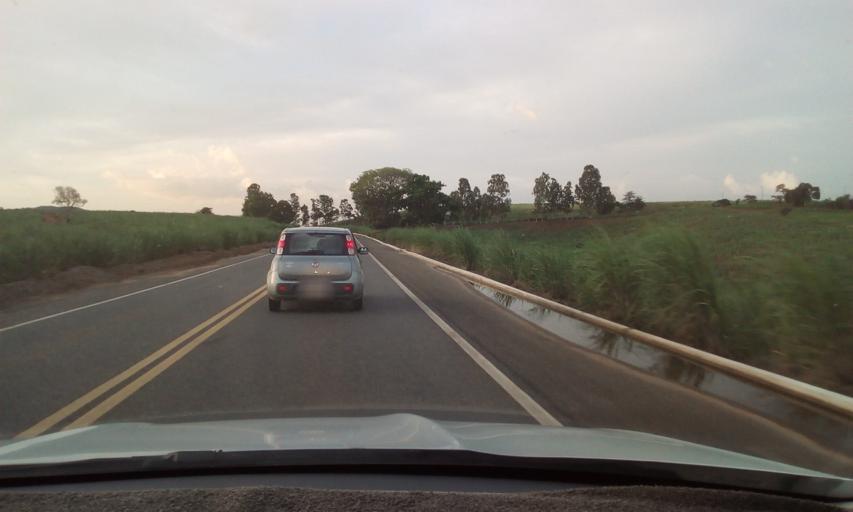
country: BR
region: Pernambuco
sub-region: Vicencia
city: Vicencia
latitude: -7.6034
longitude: -35.2409
